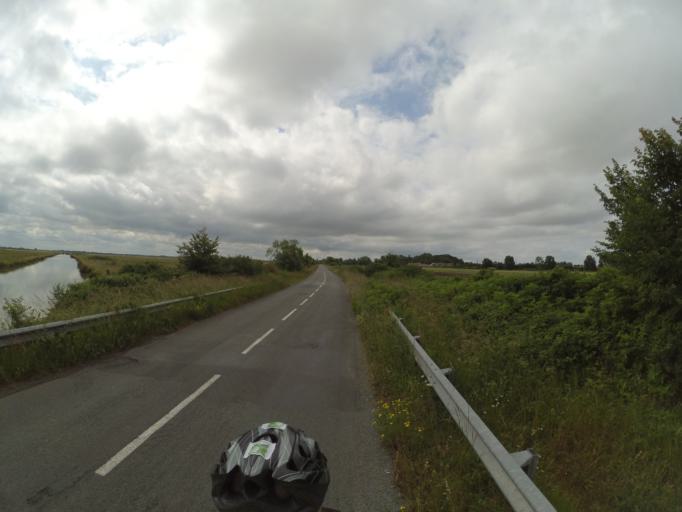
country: FR
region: Poitou-Charentes
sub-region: Departement de la Charente-Maritime
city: Yves
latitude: 46.0281
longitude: -1.0481
